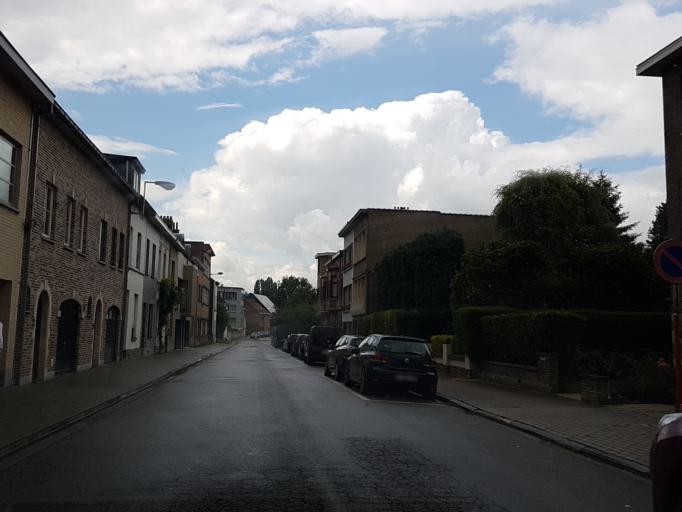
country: BE
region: Flanders
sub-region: Provincie Vlaams-Brabant
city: Grimbergen
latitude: 50.9131
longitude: 4.3503
